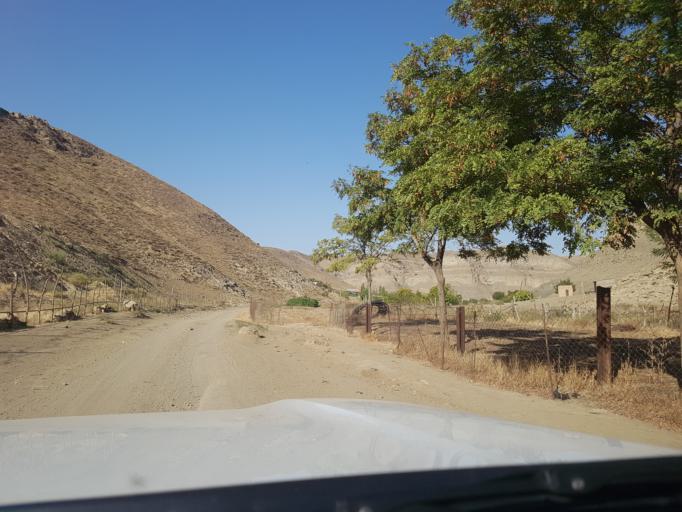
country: TM
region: Balkan
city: Magtymguly
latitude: 38.3002
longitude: 56.7544
